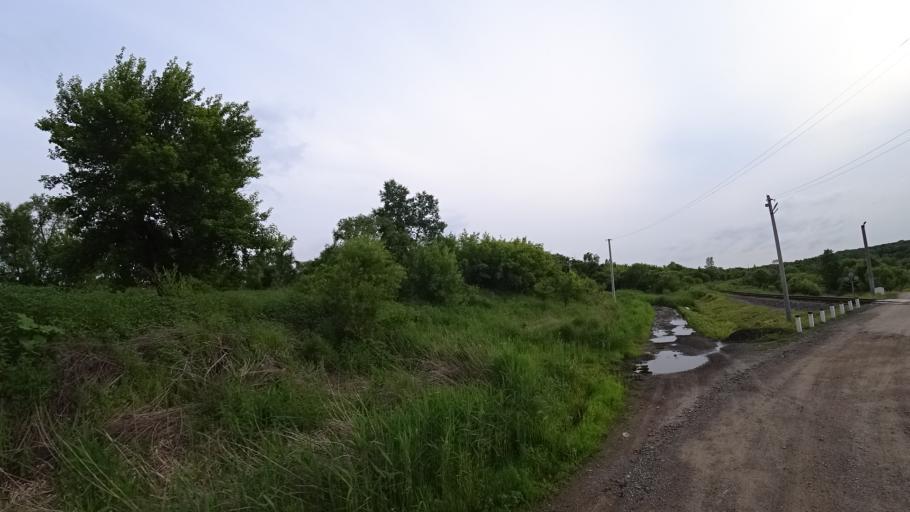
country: RU
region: Primorskiy
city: Novosysoyevka
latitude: 44.2433
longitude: 133.3653
